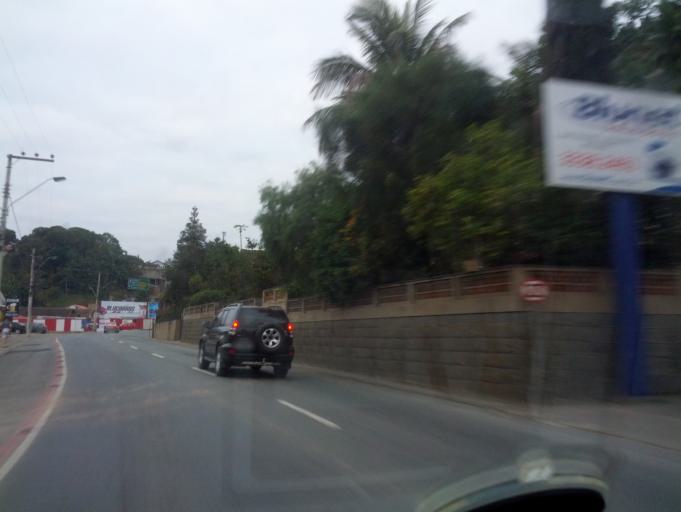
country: BR
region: Santa Catarina
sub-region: Blumenau
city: Blumenau
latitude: -26.8805
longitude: -49.0808
